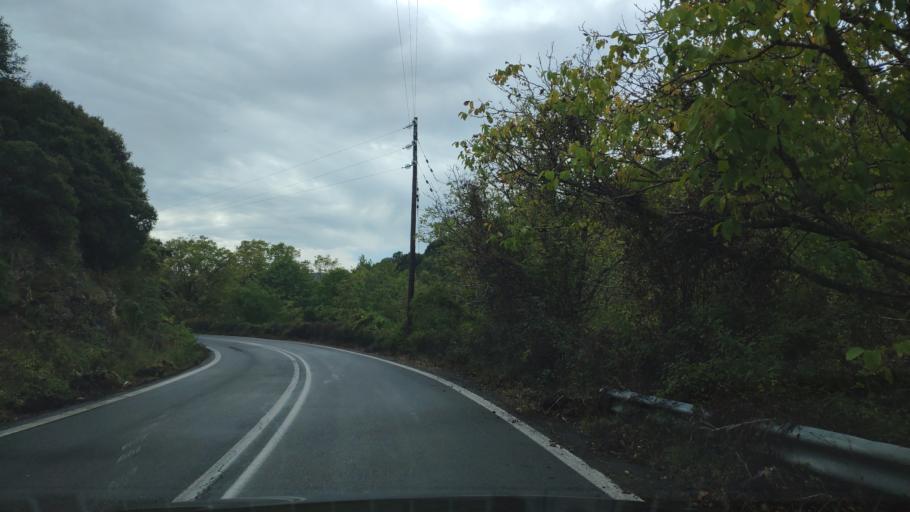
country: GR
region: Peloponnese
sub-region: Nomos Arkadias
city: Dimitsana
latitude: 37.6171
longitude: 22.0424
